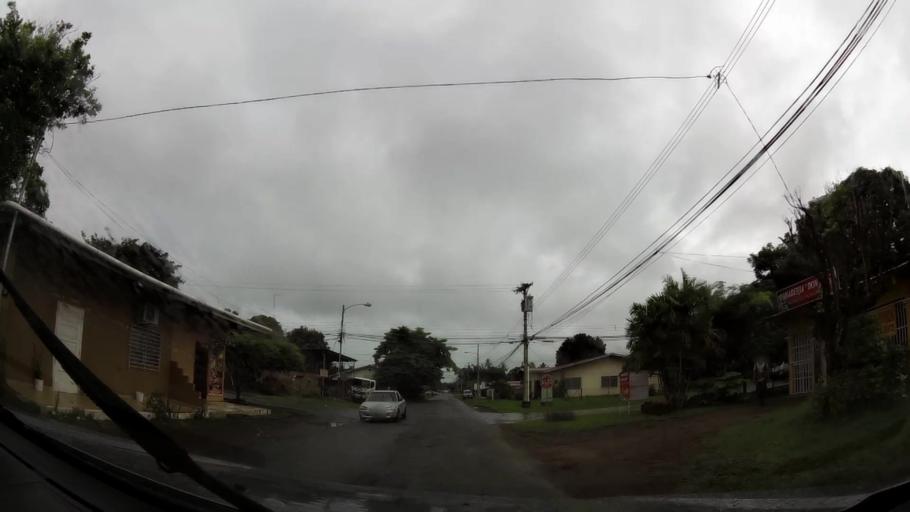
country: PA
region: Chiriqui
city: David
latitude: 8.4312
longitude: -82.4346
